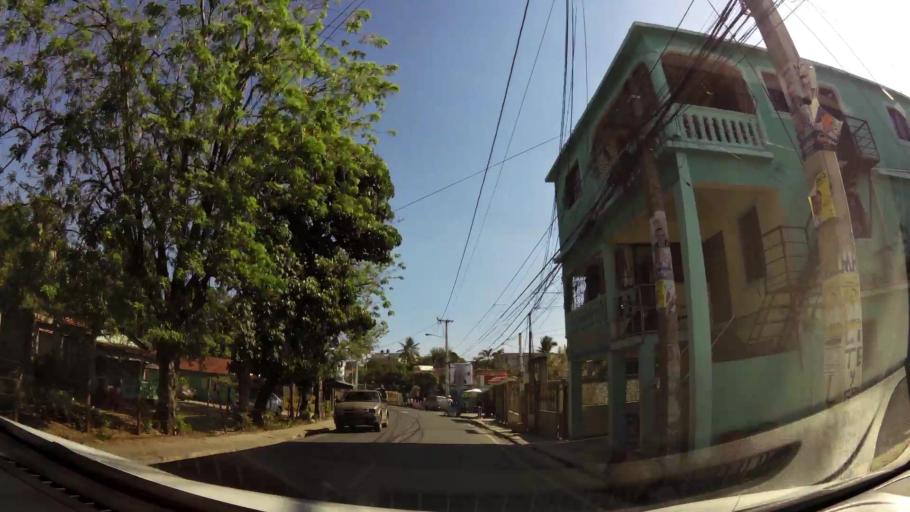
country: DO
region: Santo Domingo
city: Santo Domingo Oeste
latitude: 18.4671
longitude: -69.9986
